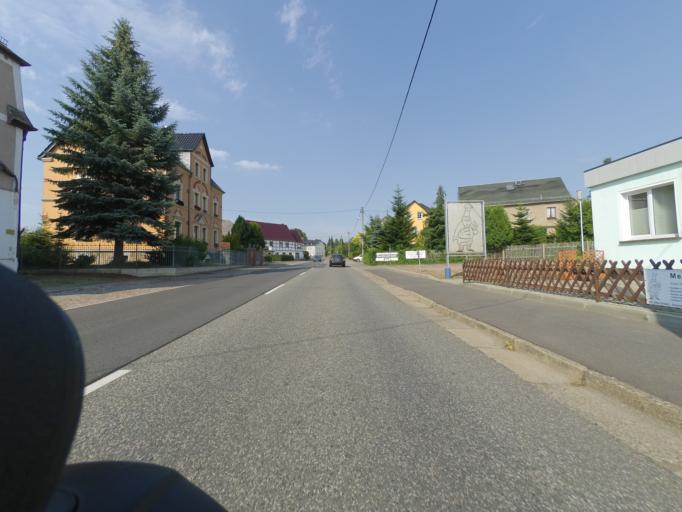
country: DE
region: Saxony
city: Geringswalde
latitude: 51.0838
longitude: 12.9201
